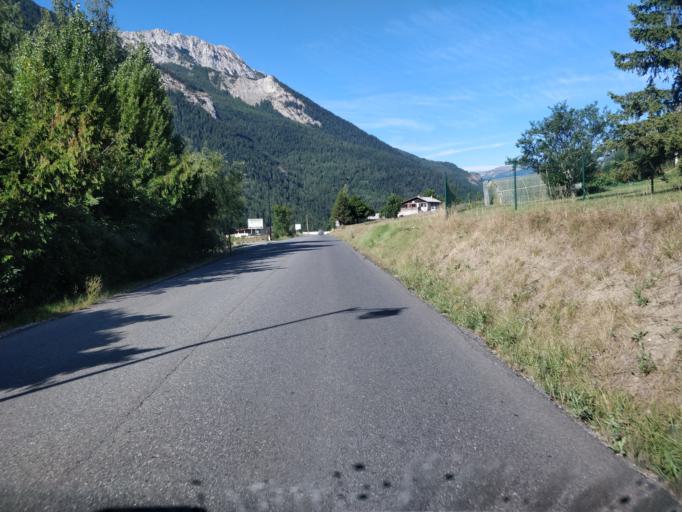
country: FR
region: Provence-Alpes-Cote d'Azur
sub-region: Departement des Alpes-de-Haute-Provence
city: Barcelonnette
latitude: 44.3930
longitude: 6.5682
